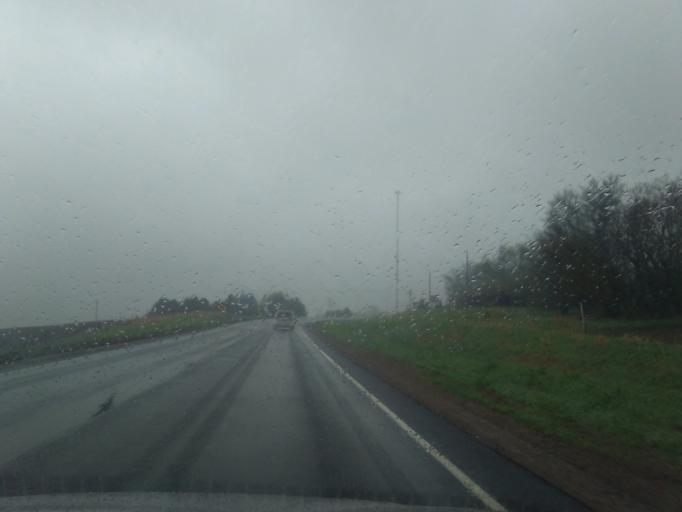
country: US
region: Nebraska
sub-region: Wayne County
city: Wayne
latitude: 42.1938
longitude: -97.1737
